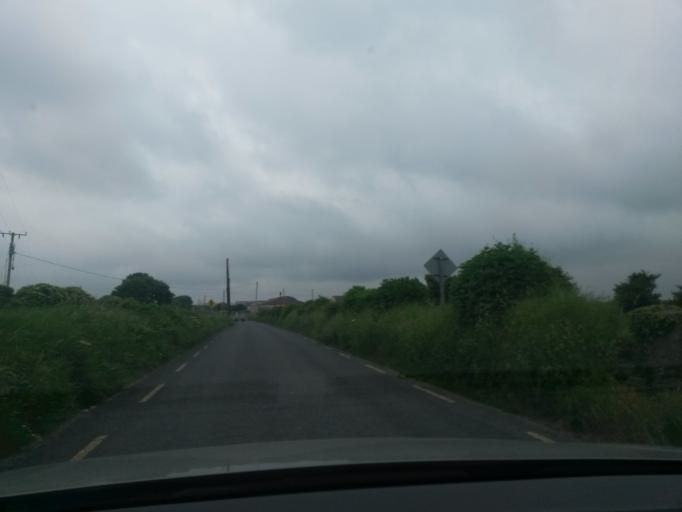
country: IE
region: Munster
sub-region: Ciarrai
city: Tralee
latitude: 52.3708
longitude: -9.7180
